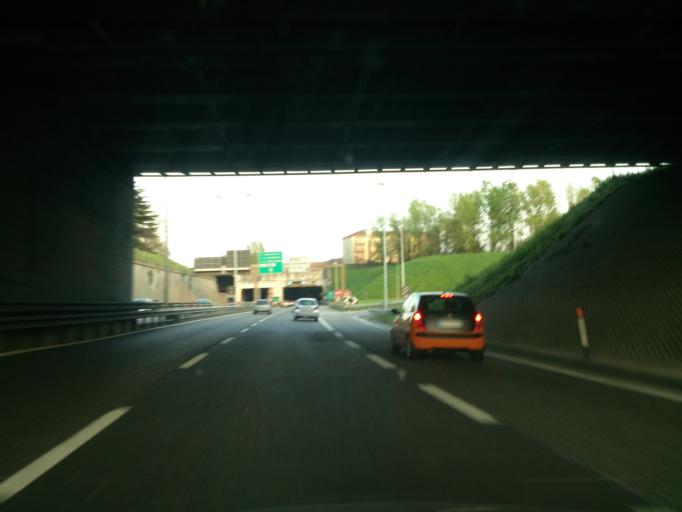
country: IT
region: Lombardy
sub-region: Provincia di Monza e Brianza
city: Monza
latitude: 45.5599
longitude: 9.2551
